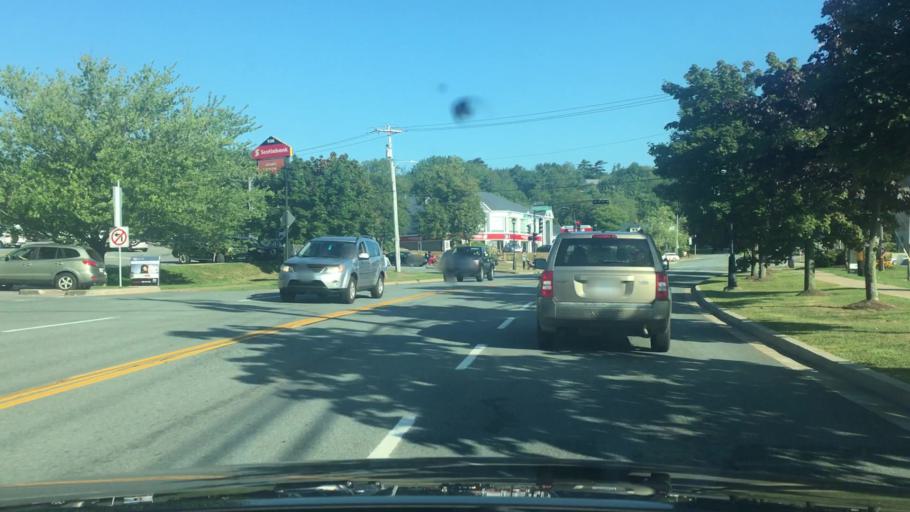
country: CA
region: Nova Scotia
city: Dartmouth
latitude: 44.7145
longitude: -63.6779
